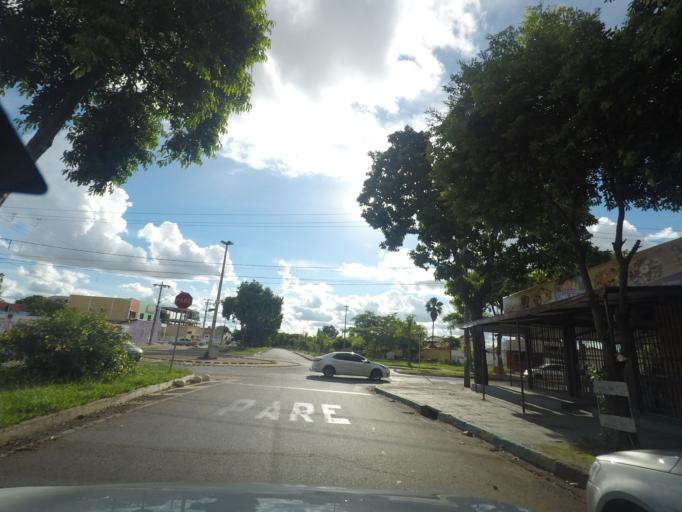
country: BR
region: Goias
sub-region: Goiania
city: Goiania
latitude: -16.7169
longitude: -49.3101
